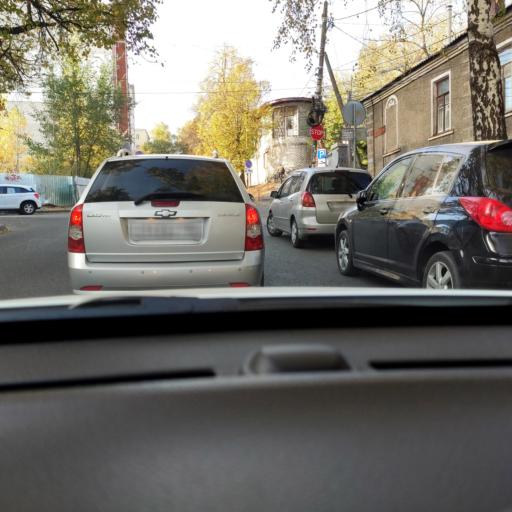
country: RU
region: Voronezj
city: Voronezh
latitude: 51.6681
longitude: 39.2127
